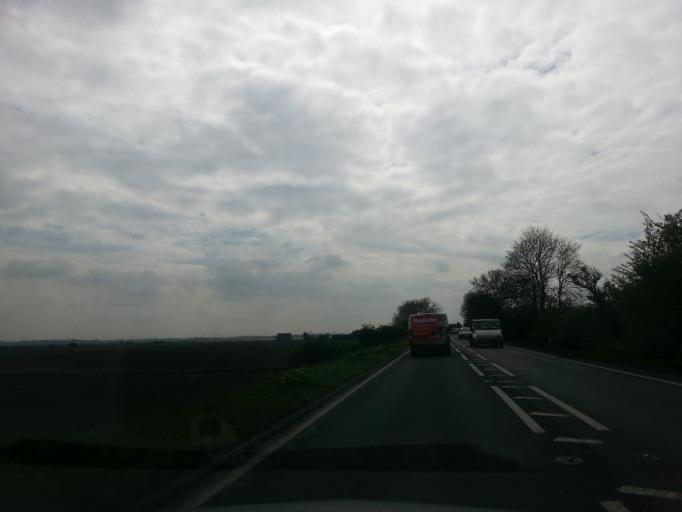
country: GB
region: England
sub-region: Cambridgeshire
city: March
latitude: 52.6197
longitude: 0.0819
